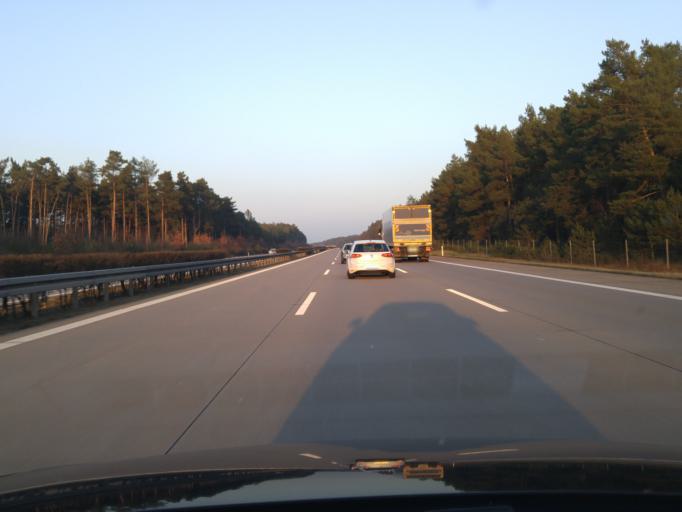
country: DE
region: Brandenburg
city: Wollin
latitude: 52.3070
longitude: 12.4789
